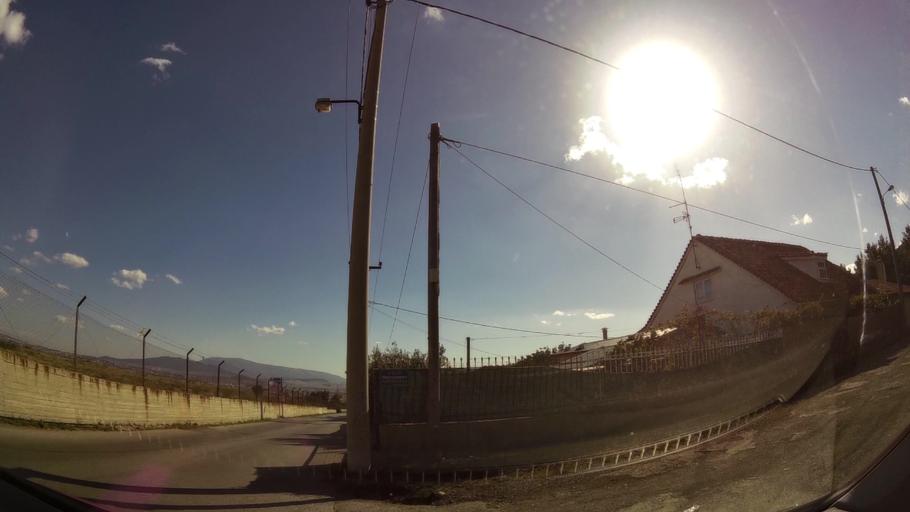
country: GR
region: Attica
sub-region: Nomarchia Anatolikis Attikis
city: Acharnes
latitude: 38.1101
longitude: 23.7223
